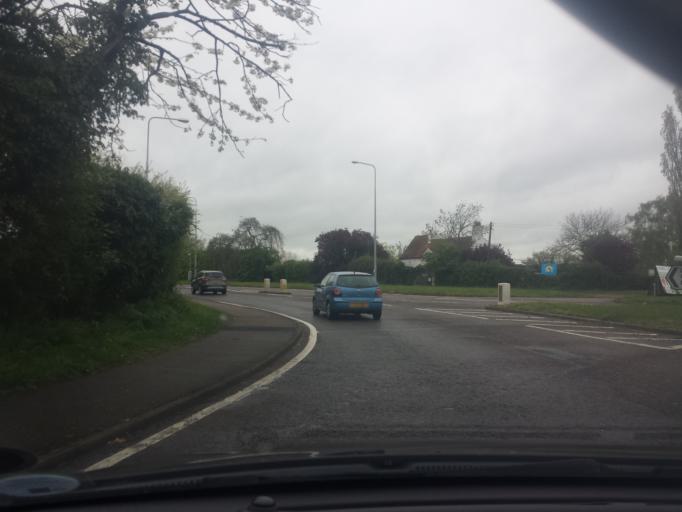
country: GB
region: England
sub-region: Essex
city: Great Bentley
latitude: 51.8590
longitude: 1.1088
